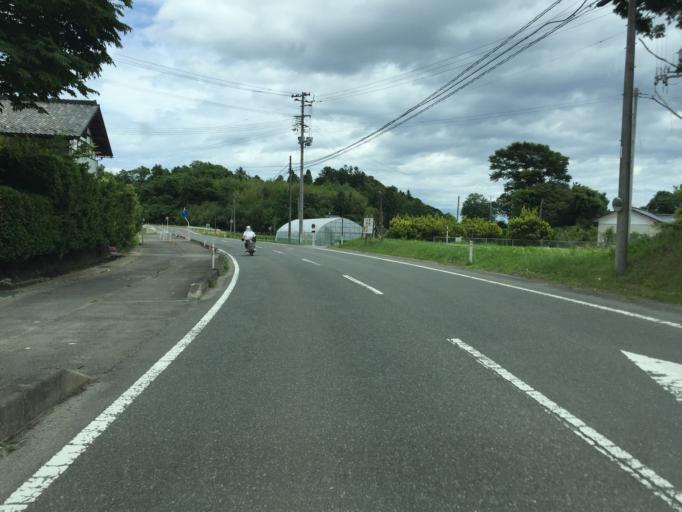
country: JP
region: Fukushima
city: Namie
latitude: 37.6810
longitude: 140.9686
